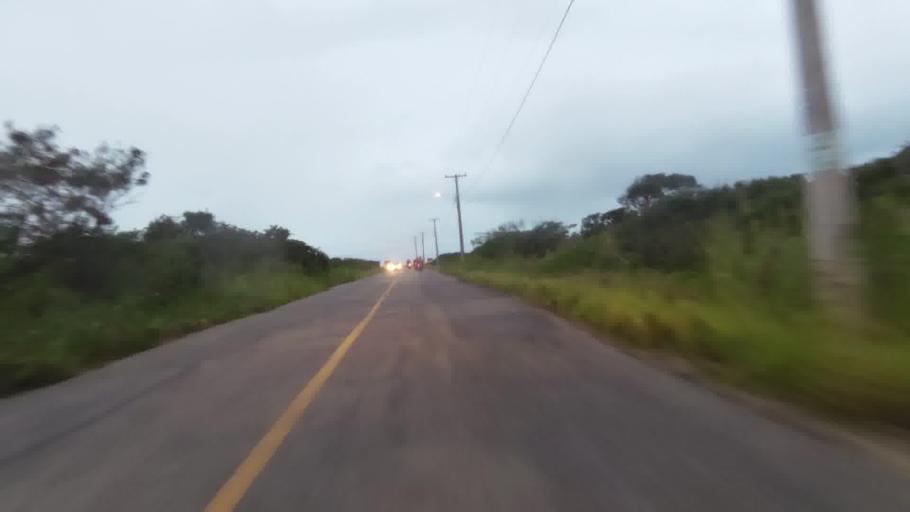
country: BR
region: Espirito Santo
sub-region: Itapemirim
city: Itapemirim
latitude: -20.9794
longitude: -40.8136
